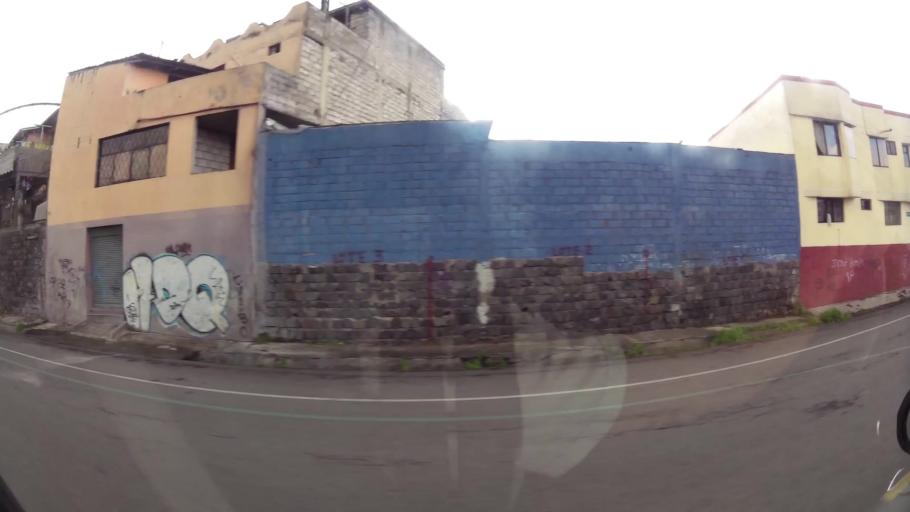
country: EC
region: Pichincha
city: Sangolqui
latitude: -0.3351
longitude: -78.4420
